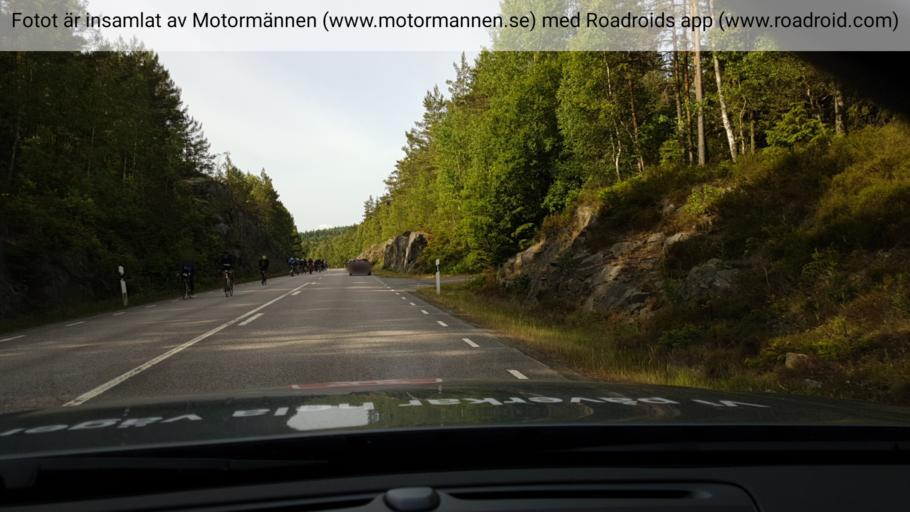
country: SE
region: Vaestra Goetaland
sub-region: Karlsborgs Kommun
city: Karlsborg
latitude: 58.6264
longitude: 14.5364
